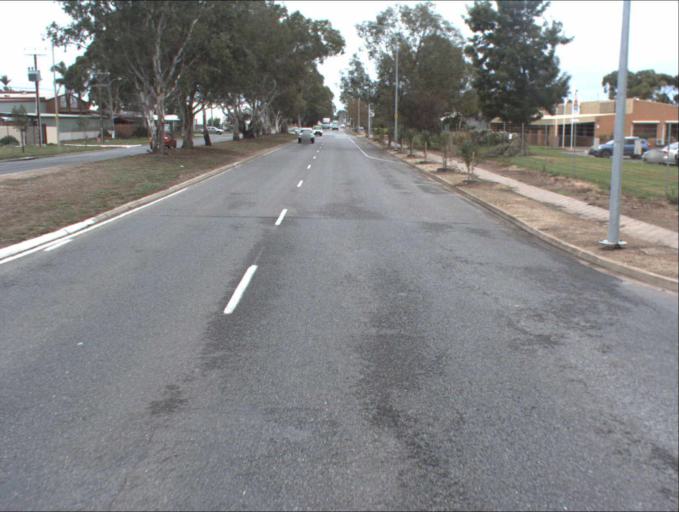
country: AU
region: South Australia
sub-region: Port Adelaide Enfield
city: Enfield
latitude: -34.8404
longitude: 138.5923
